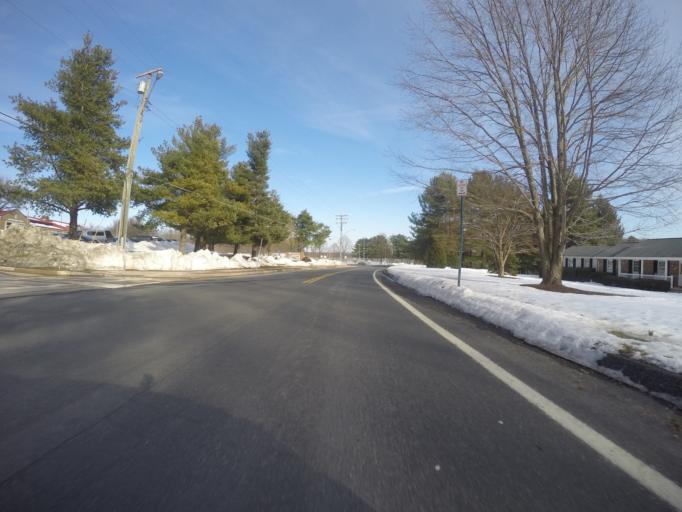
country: US
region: Maryland
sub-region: Baltimore County
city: Hunt Valley
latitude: 39.5716
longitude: -76.6538
